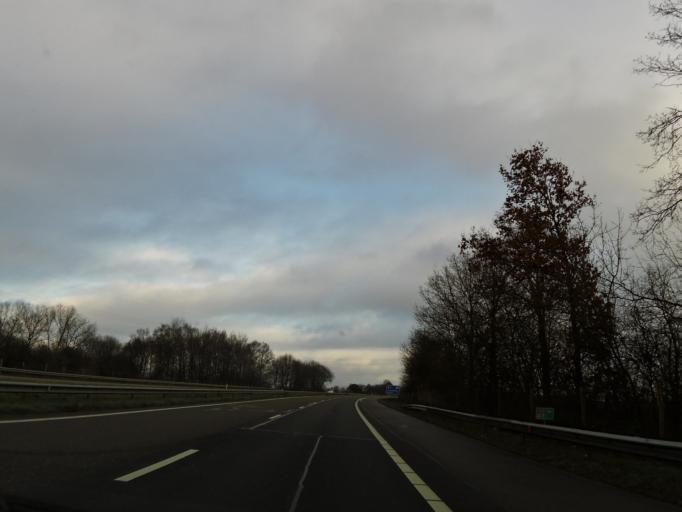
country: NL
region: Limburg
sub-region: Valkenburg aan de Geul
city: Valkenburg
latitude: 50.8811
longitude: 5.8383
